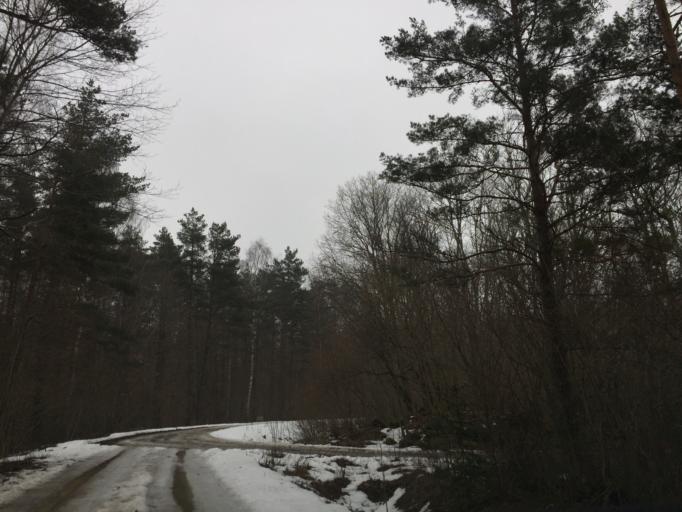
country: EE
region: Saare
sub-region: Kuressaare linn
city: Kuressaare
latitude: 58.2756
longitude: 22.5686
